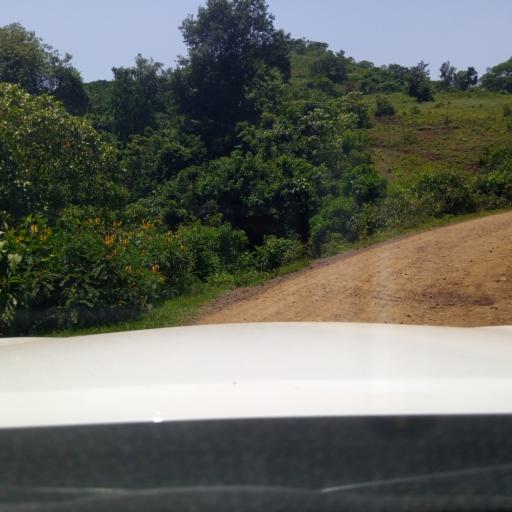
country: ET
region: Oromiya
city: Agaro
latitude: 8.1553
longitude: 36.9231
